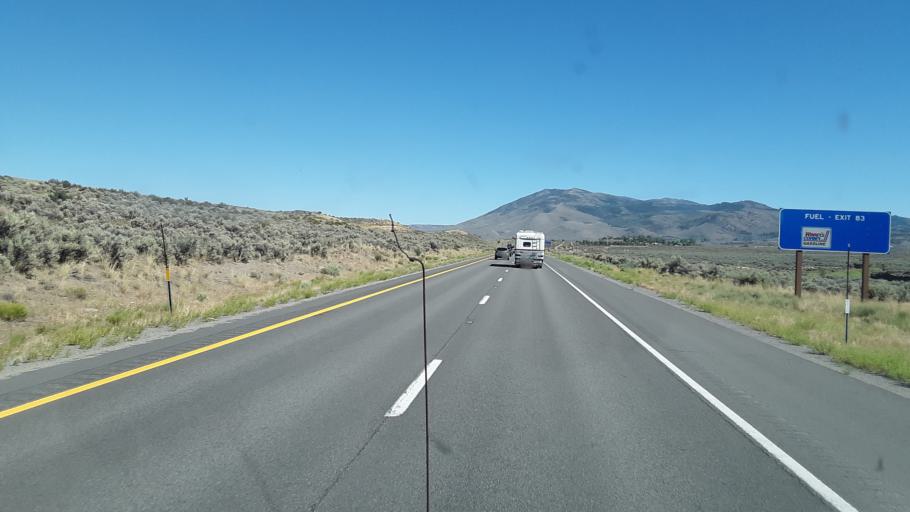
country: US
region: Nevada
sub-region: Washoe County
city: Cold Springs
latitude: 39.6814
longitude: -120.0097
